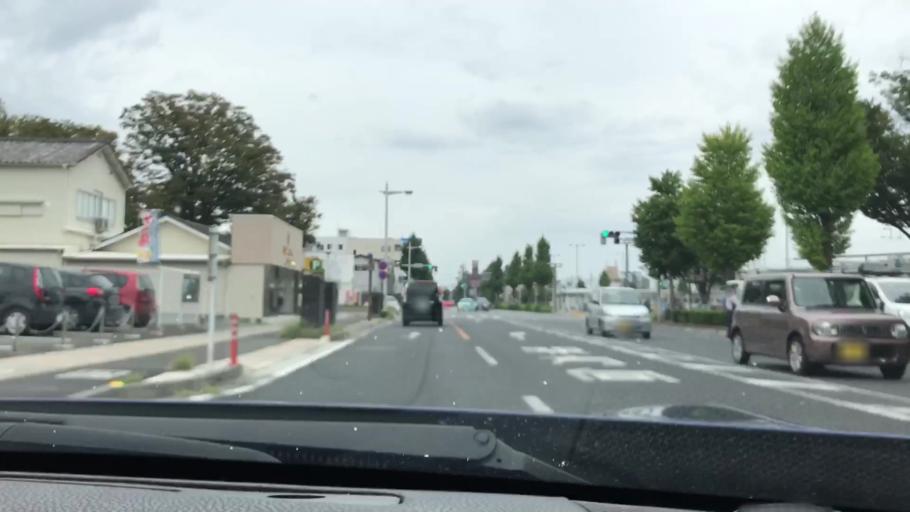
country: JP
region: Gunma
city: Maebashi-shi
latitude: 36.3843
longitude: 139.0718
